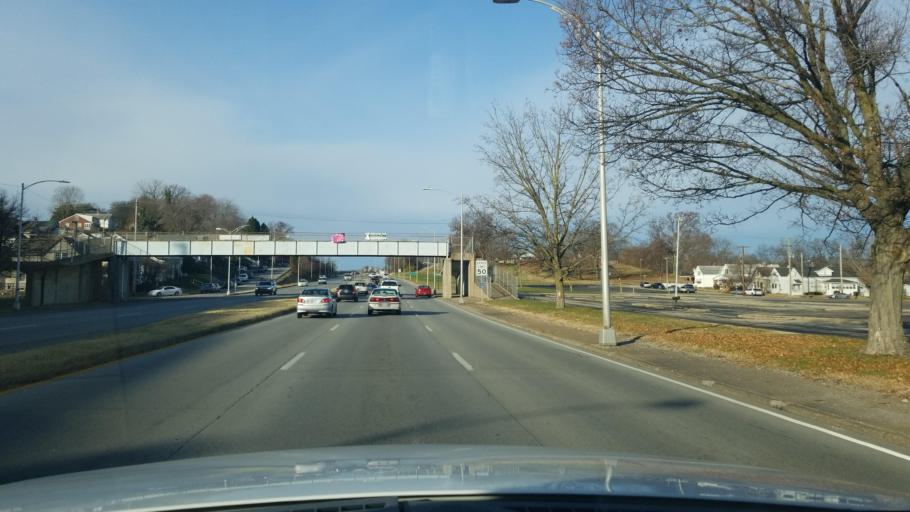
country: US
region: Indiana
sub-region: Vanderburgh County
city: Evansville
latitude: 37.9780
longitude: -87.6022
